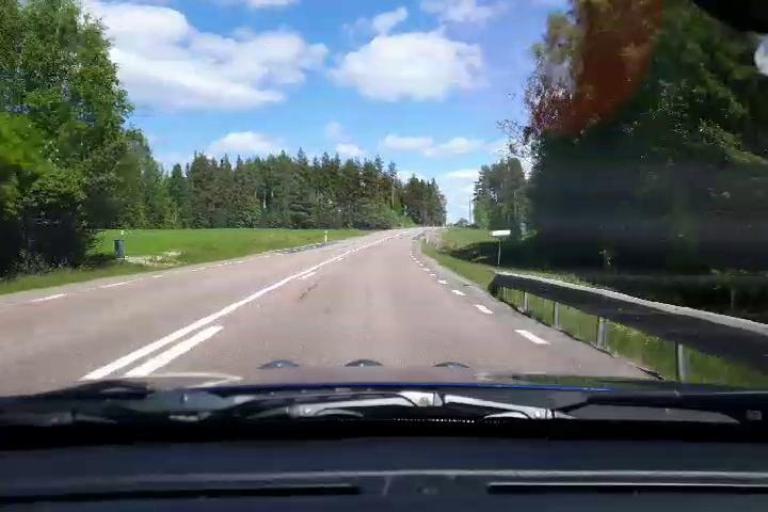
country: SE
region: Gaevleborg
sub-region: Ljusdals Kommun
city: Farila
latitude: 61.8129
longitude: 15.9602
